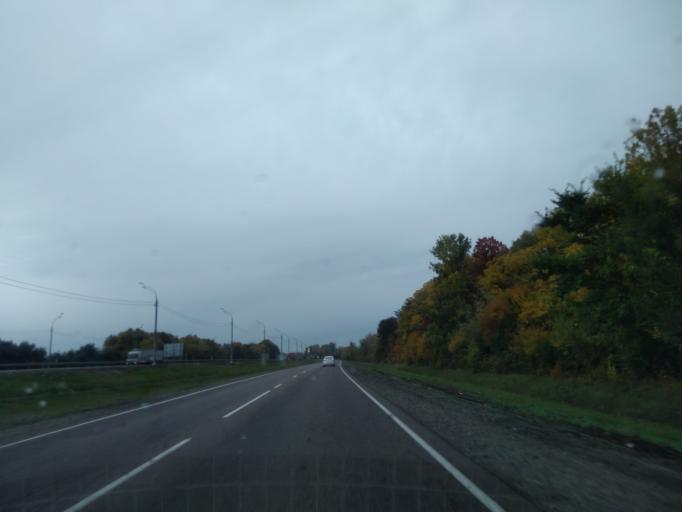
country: RU
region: Lipetsk
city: Zadonsk
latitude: 52.4385
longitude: 38.8114
